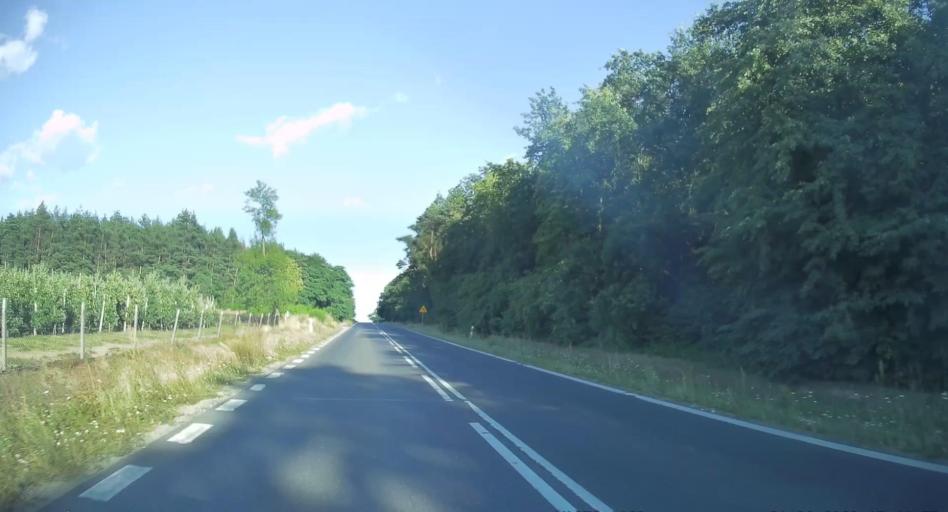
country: PL
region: Lodz Voivodeship
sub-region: Powiat rawski
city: Biala Rawska
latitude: 51.8011
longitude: 20.5124
